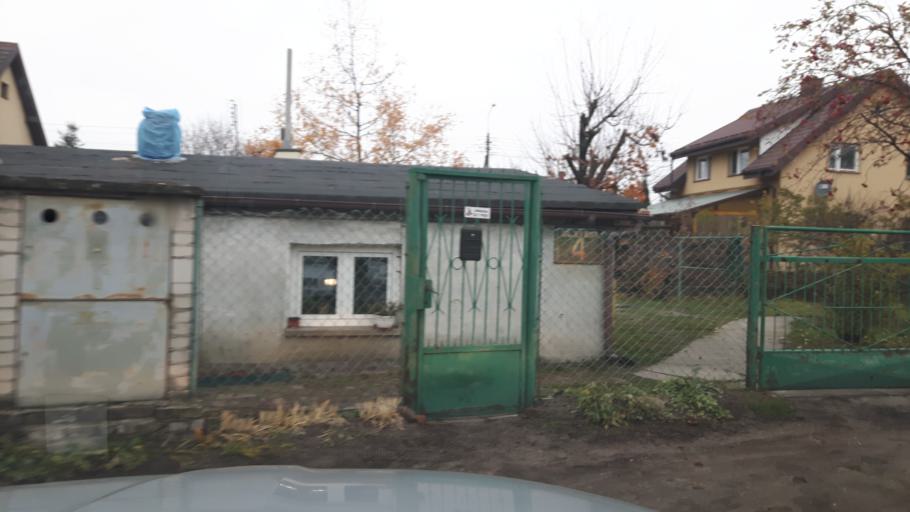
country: PL
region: Masovian Voivodeship
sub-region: Powiat wolominski
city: Zabki
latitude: 52.2820
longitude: 21.1090
